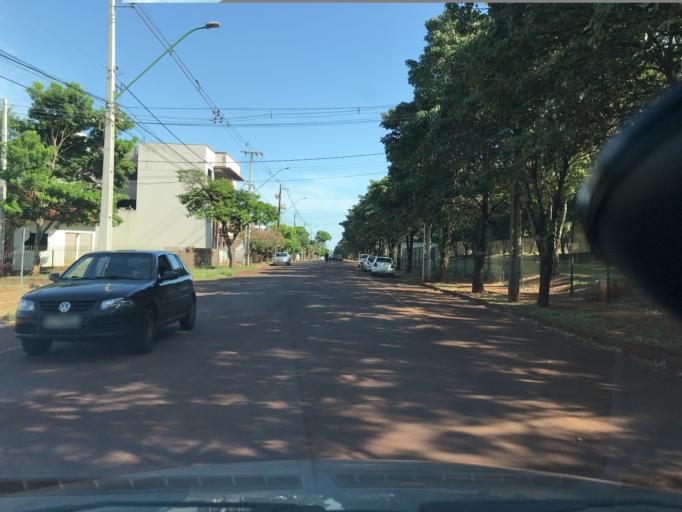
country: BR
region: Parana
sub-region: Palotina
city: Palotina
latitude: -24.2959
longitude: -53.8433
